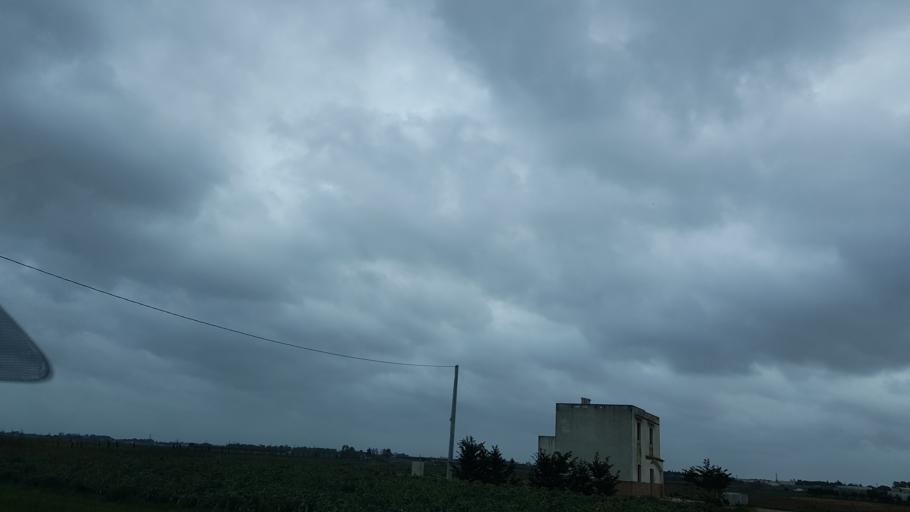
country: IT
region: Apulia
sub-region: Provincia di Brindisi
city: Brindisi
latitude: 40.6591
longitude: 17.8644
